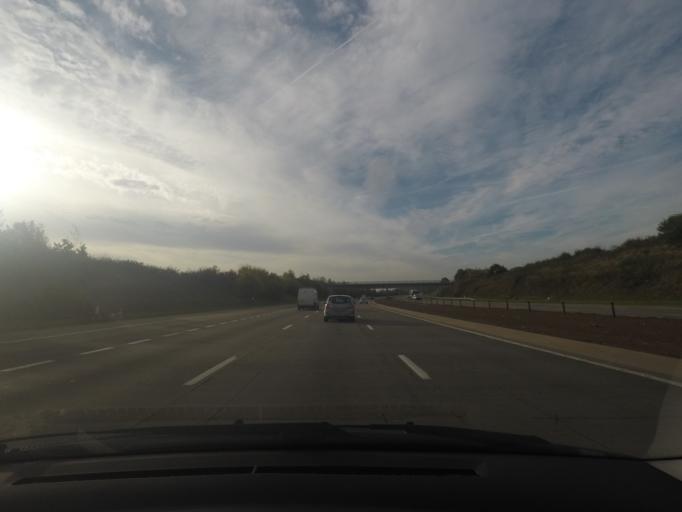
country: GB
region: England
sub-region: City and Borough of Leeds
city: Swillington
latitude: 53.7822
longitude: -1.4280
